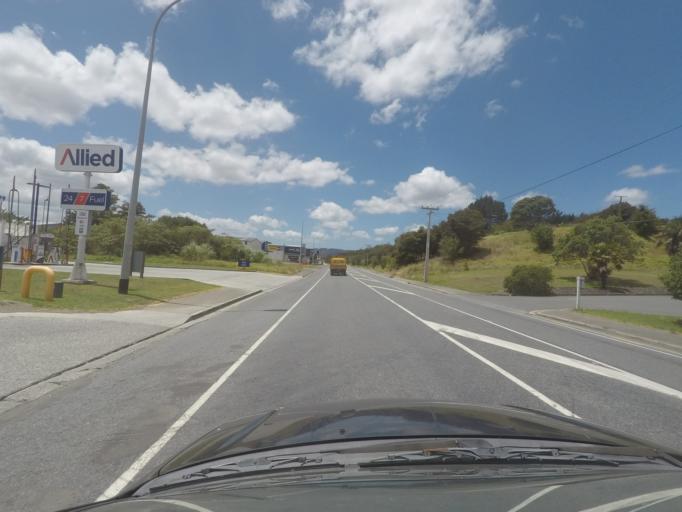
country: NZ
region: Northland
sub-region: Whangarei
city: Whangarei
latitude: -35.7437
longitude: 174.3284
